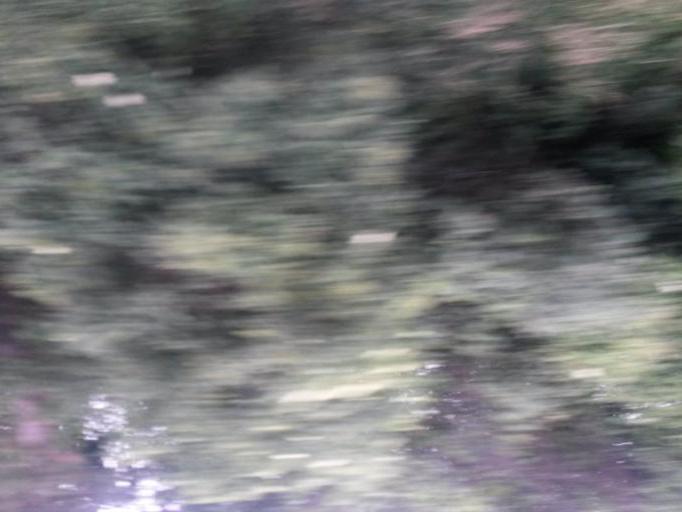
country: CZ
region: Olomoucky
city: Hnevotin
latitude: 49.5580
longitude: 17.1928
